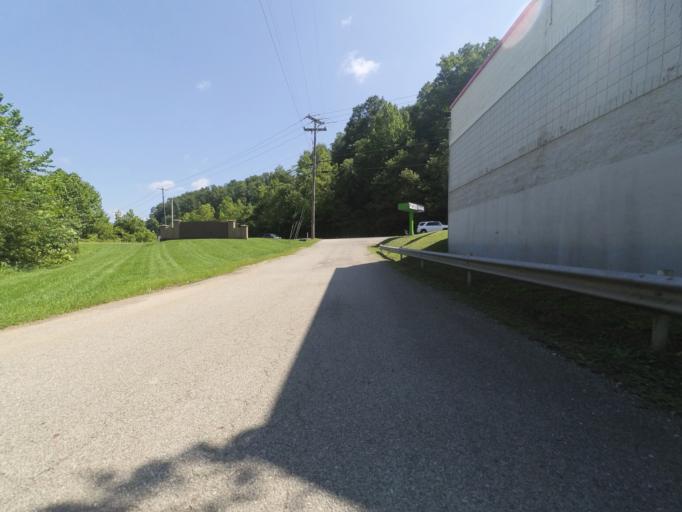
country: US
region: West Virginia
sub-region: Cabell County
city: Huntington
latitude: 38.3823
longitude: -82.4574
